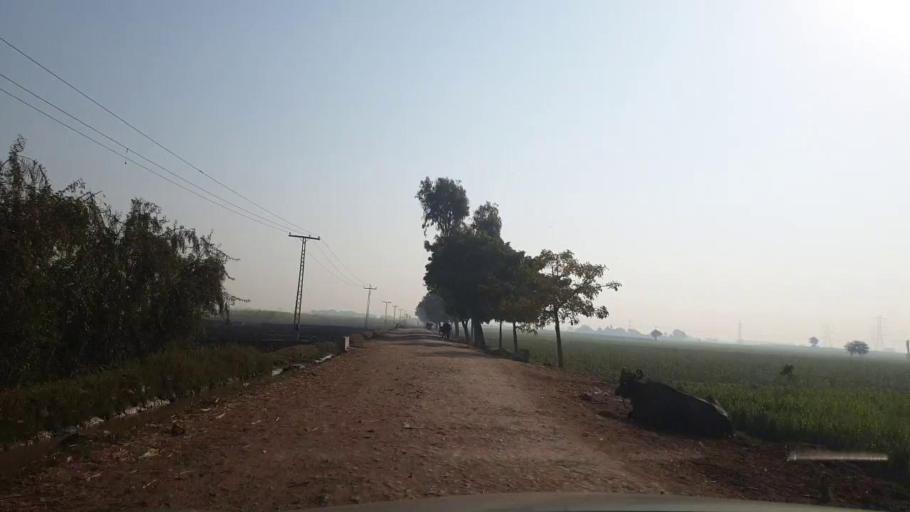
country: PK
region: Sindh
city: Tando Allahyar
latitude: 25.4919
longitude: 68.7218
